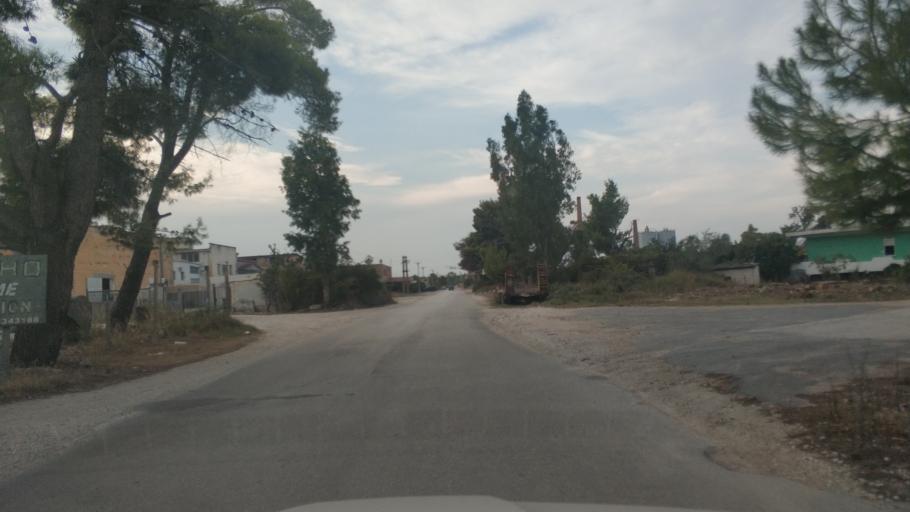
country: AL
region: Vlore
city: Vlore
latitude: 40.4717
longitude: 19.4580
